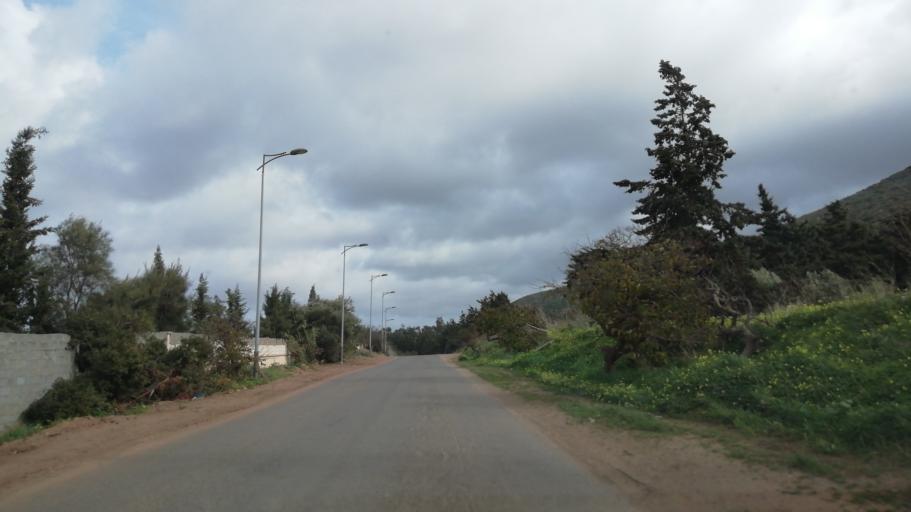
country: DZ
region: Oran
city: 'Ain el Turk
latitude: 35.6946
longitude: -0.8566
